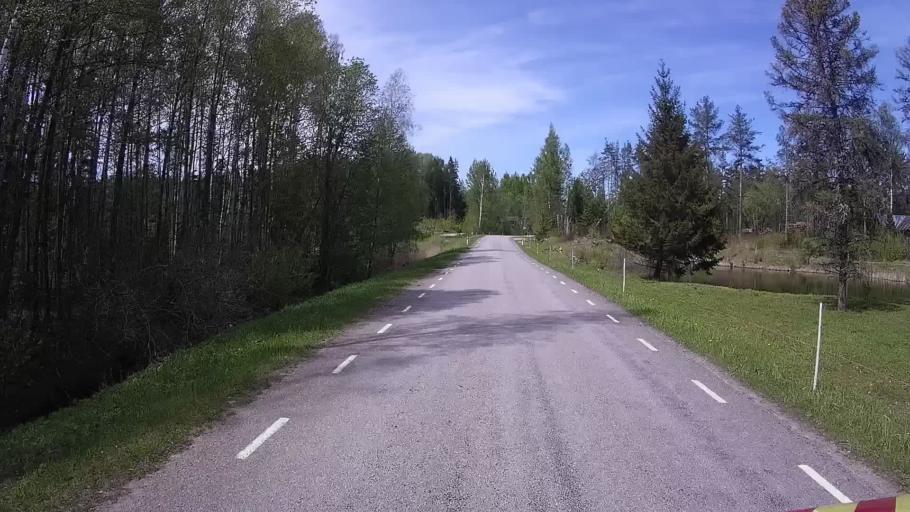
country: EE
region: Vorumaa
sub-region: Antsla vald
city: Vana-Antsla
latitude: 57.6224
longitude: 26.3491
